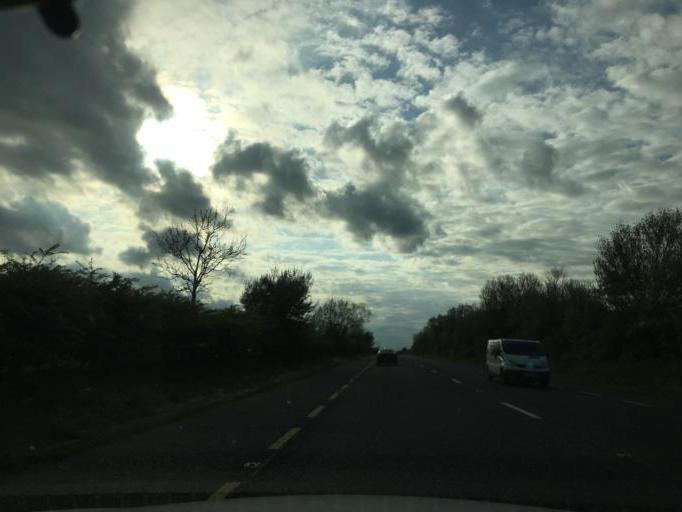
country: IE
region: Leinster
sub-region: Loch Garman
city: Loch Garman
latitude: 52.3413
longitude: -6.5726
